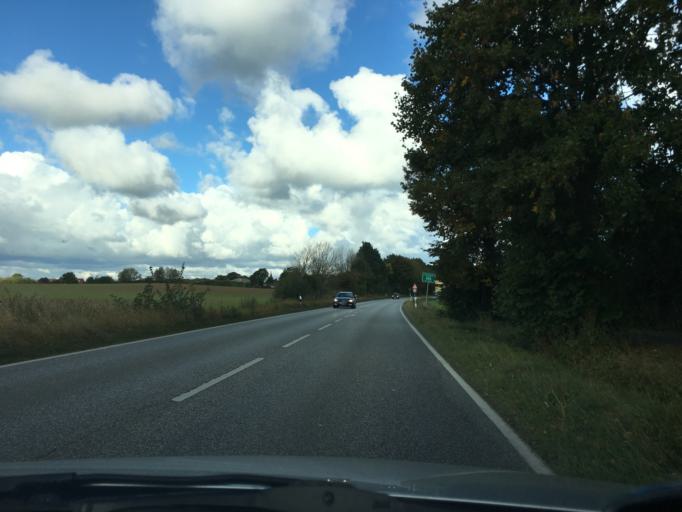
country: DE
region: Schleswig-Holstein
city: Brodersdorf
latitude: 54.3950
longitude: 10.2379
